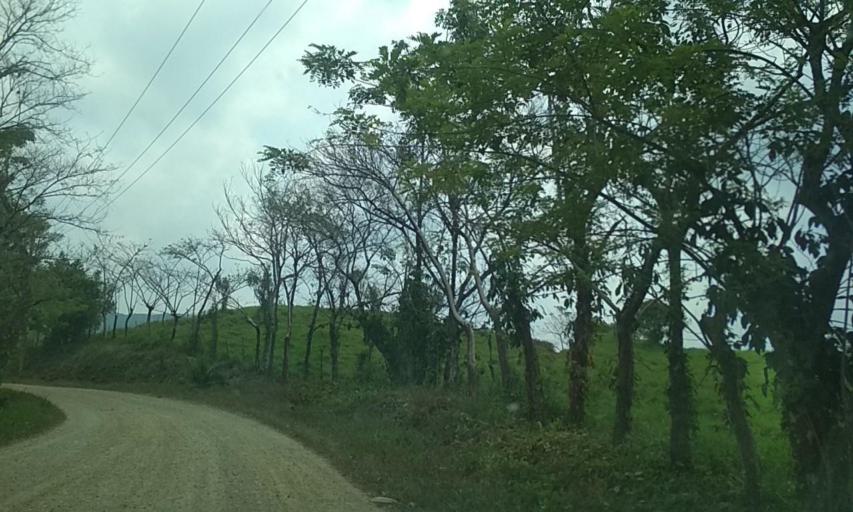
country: MX
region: Tabasco
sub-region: Huimanguillo
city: Francisco Rueda
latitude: 17.6015
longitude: -93.8018
